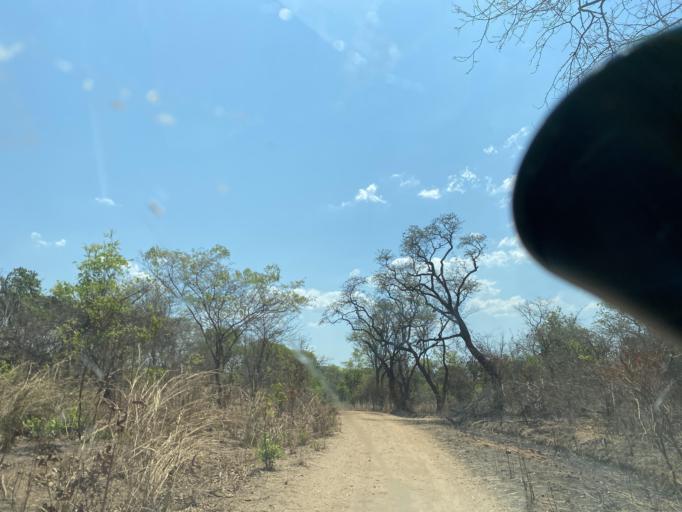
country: ZM
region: Lusaka
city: Chongwe
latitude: -15.0877
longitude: 29.4950
